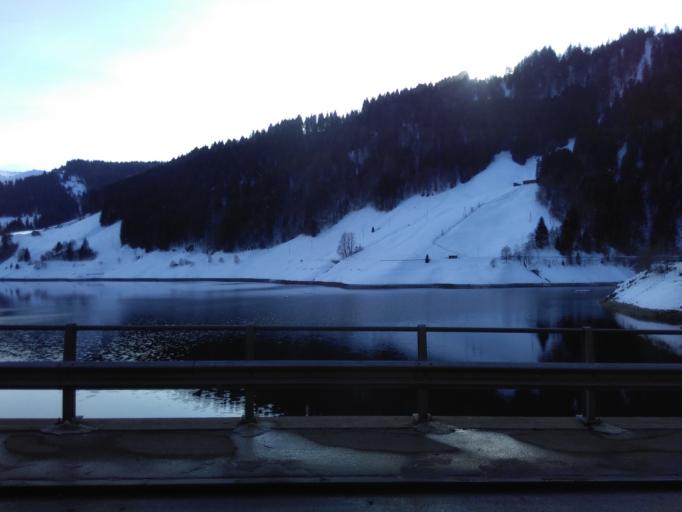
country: CH
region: Schwyz
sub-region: Bezirk March
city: Vorderthal
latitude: 47.1068
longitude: 8.9059
